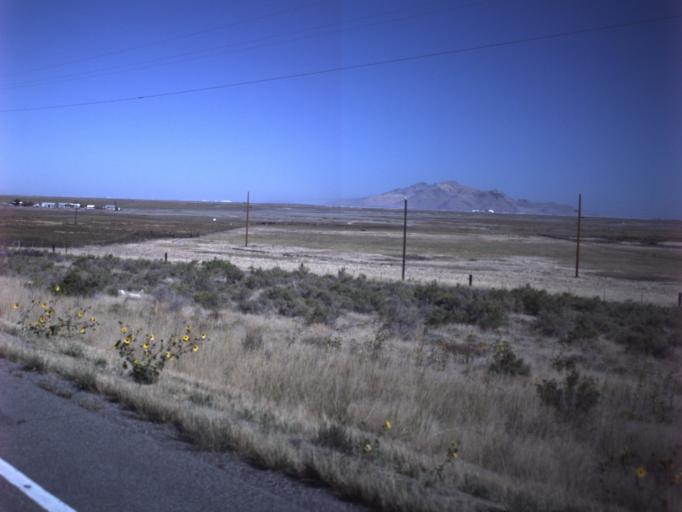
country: US
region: Utah
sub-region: Tooele County
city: Grantsville
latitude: 40.6375
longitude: -112.5208
